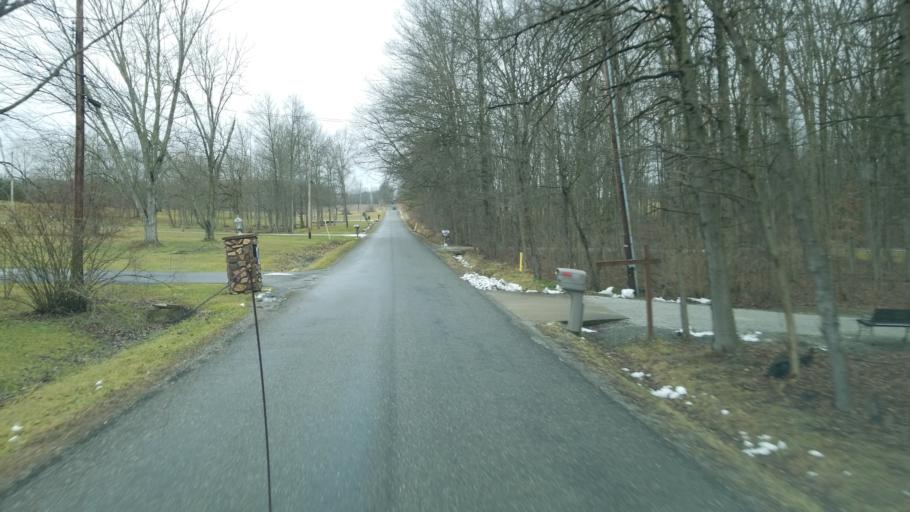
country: US
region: Ohio
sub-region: Portage County
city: Windham
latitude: 41.3394
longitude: -80.9788
